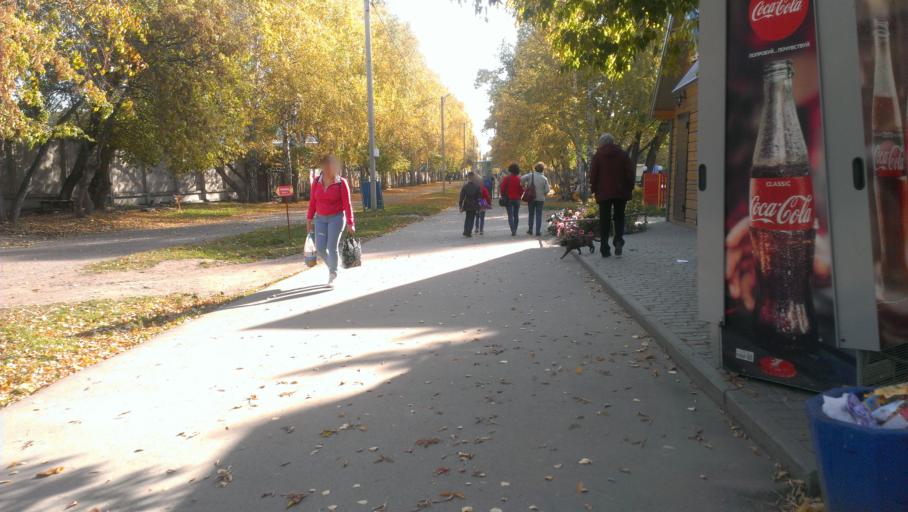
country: RU
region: Altai Krai
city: Novosilikatnyy
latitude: 53.3573
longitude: 83.6847
